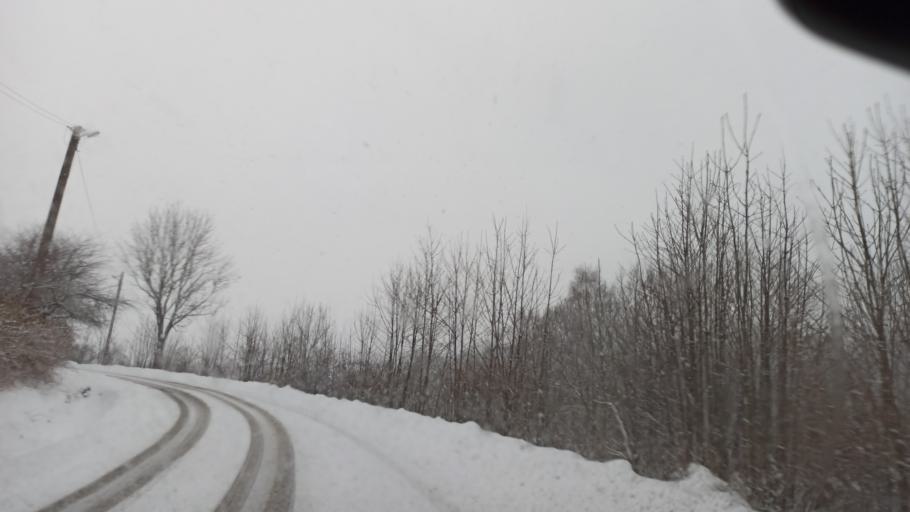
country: PL
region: Lower Silesian Voivodeship
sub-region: Powiat klodzki
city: Ludwikowice Klodzkie
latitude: 50.6513
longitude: 16.4727
